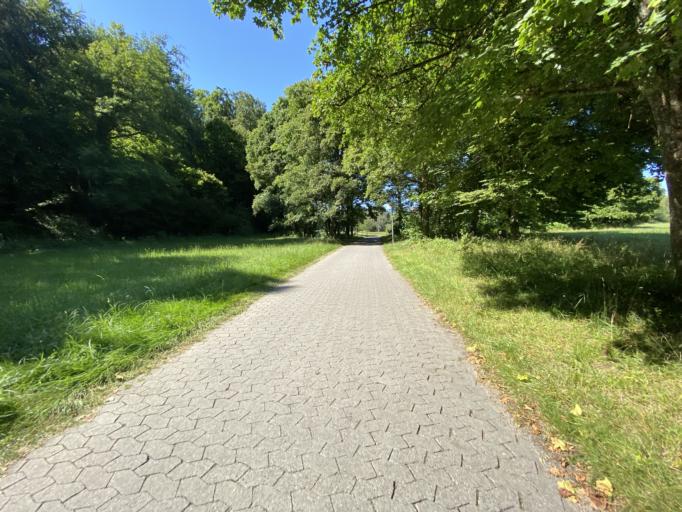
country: DE
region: Baden-Wuerttemberg
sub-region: Freiburg Region
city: Konstanz
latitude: 47.6852
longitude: 9.1892
